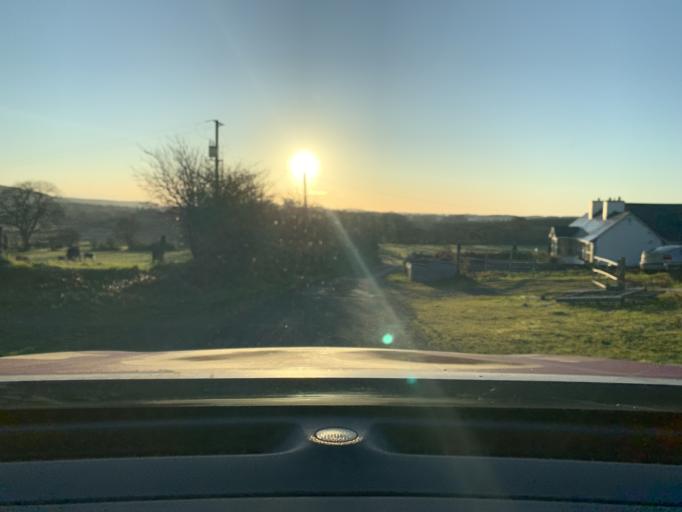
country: IE
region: Connaught
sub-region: Sligo
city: Ballymote
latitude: 54.0636
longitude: -8.5312
